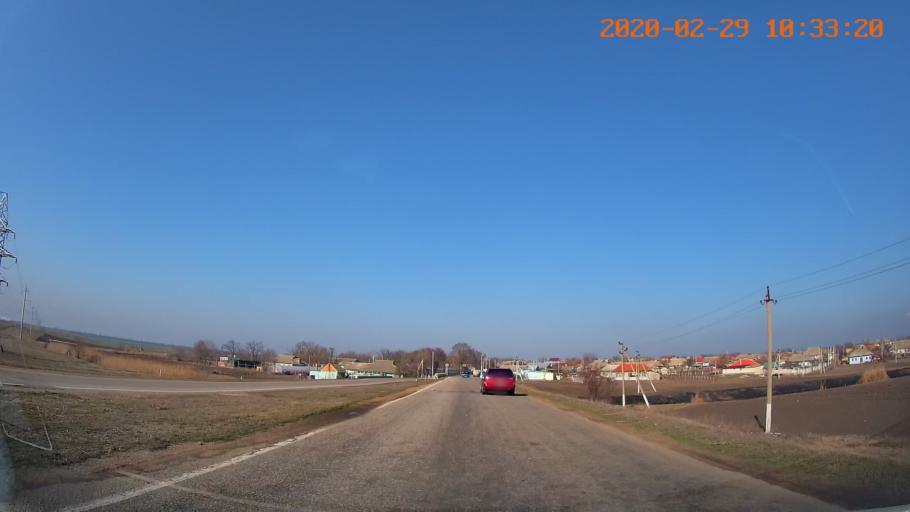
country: MD
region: Anenii Noi
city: Varnita
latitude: 46.9700
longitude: 29.5457
